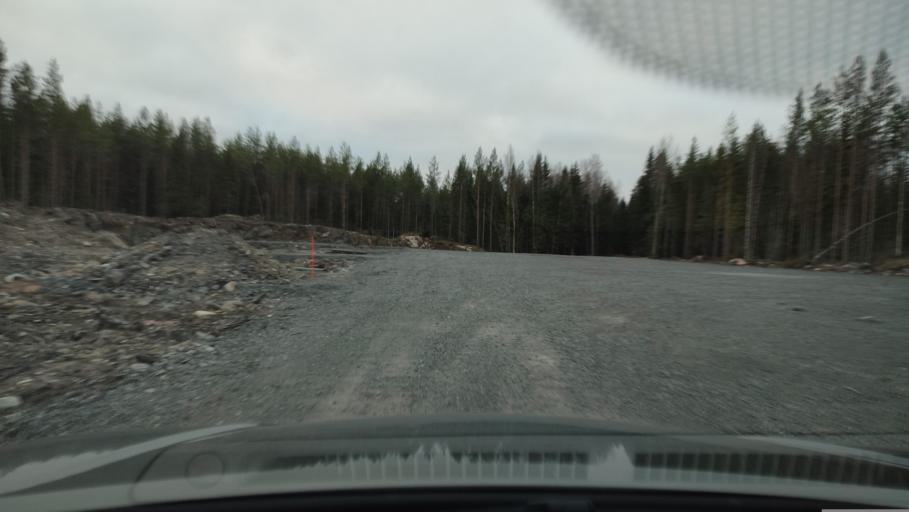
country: FI
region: Southern Ostrobothnia
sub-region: Suupohja
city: Karijoki
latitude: 62.1804
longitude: 21.5708
